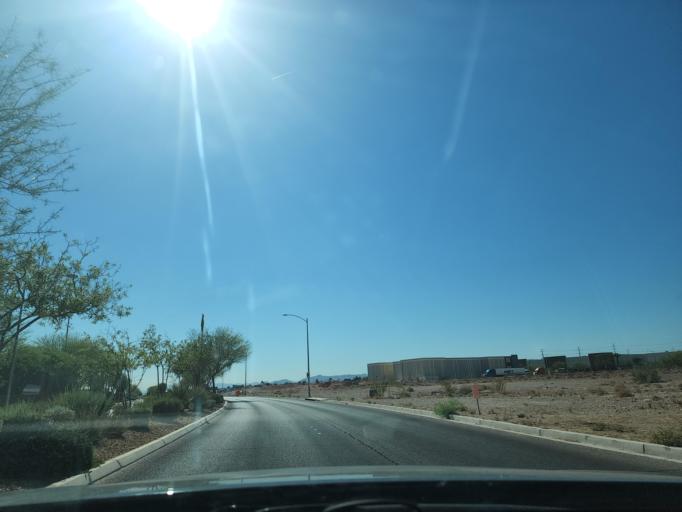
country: US
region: Nevada
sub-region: Clark County
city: Enterprise
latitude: 36.0614
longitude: -115.2494
